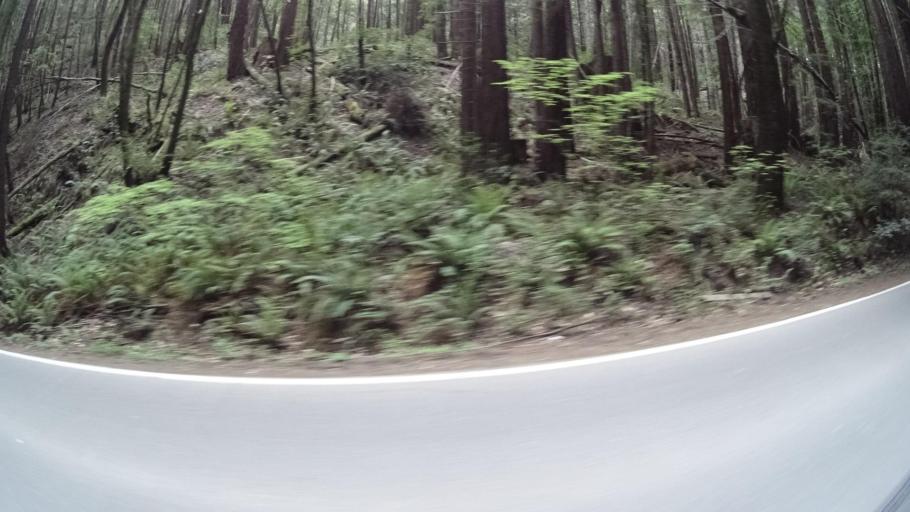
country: US
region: California
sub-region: Humboldt County
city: Redway
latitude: 40.1237
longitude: -123.8454
